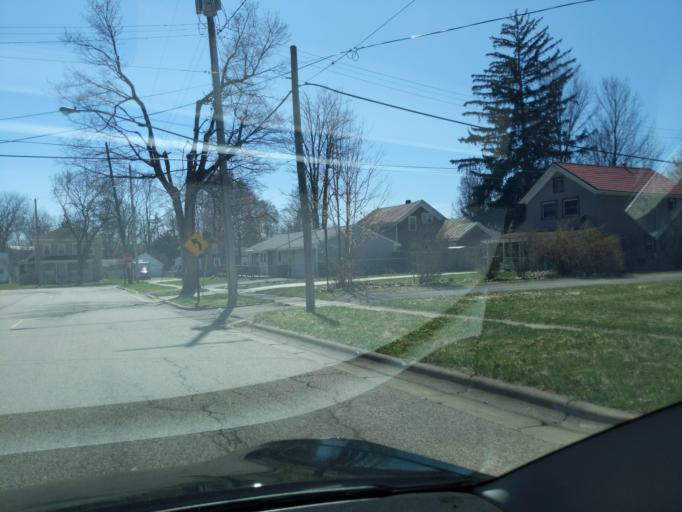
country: US
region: Michigan
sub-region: Ingham County
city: Mason
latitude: 42.5759
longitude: -84.4415
